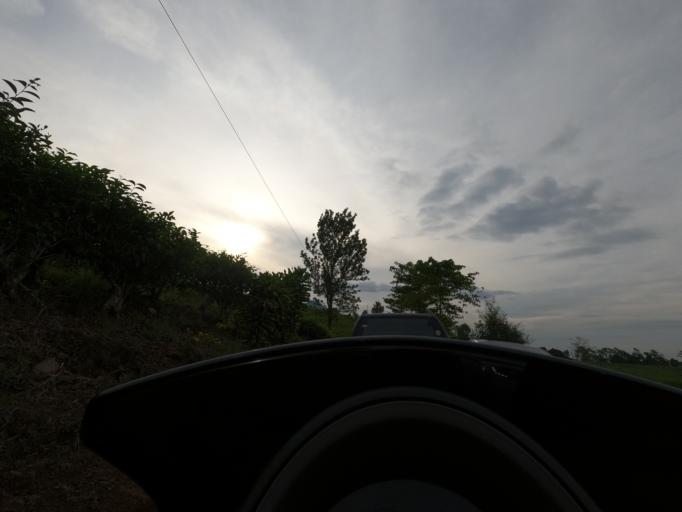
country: ID
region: West Java
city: Lembang
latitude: -6.7301
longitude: 107.6441
